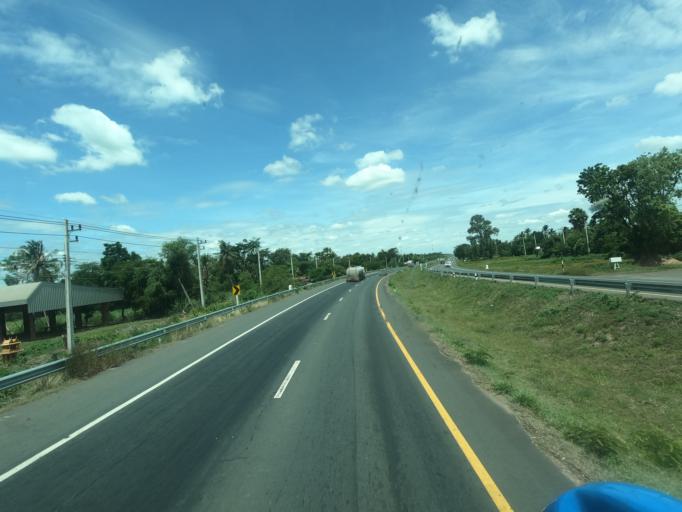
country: TH
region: Surin
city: Prasat
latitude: 14.6088
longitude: 103.3217
